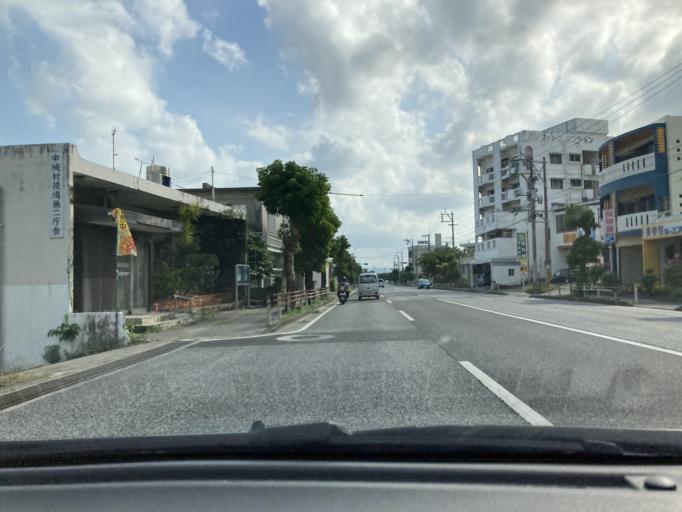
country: JP
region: Okinawa
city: Ginowan
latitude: 26.2674
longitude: 127.7907
